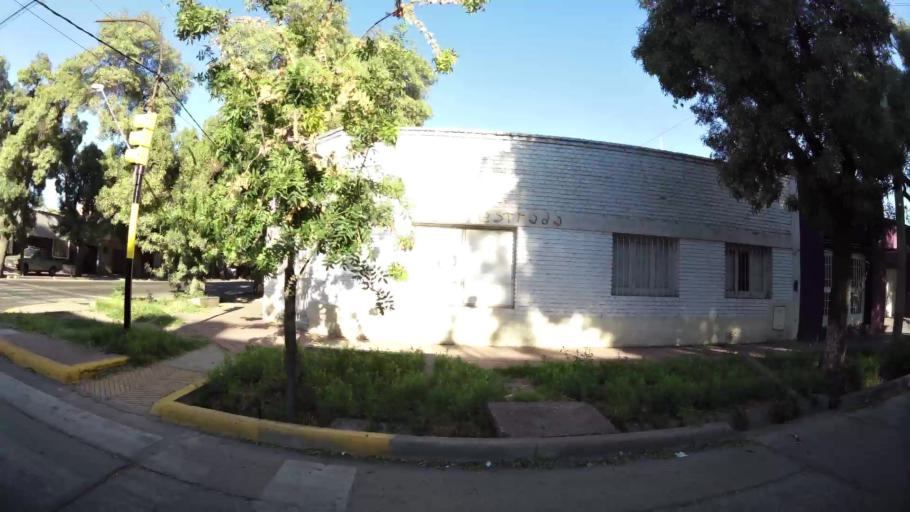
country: AR
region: Mendoza
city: Las Heras
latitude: -32.8709
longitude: -68.8232
